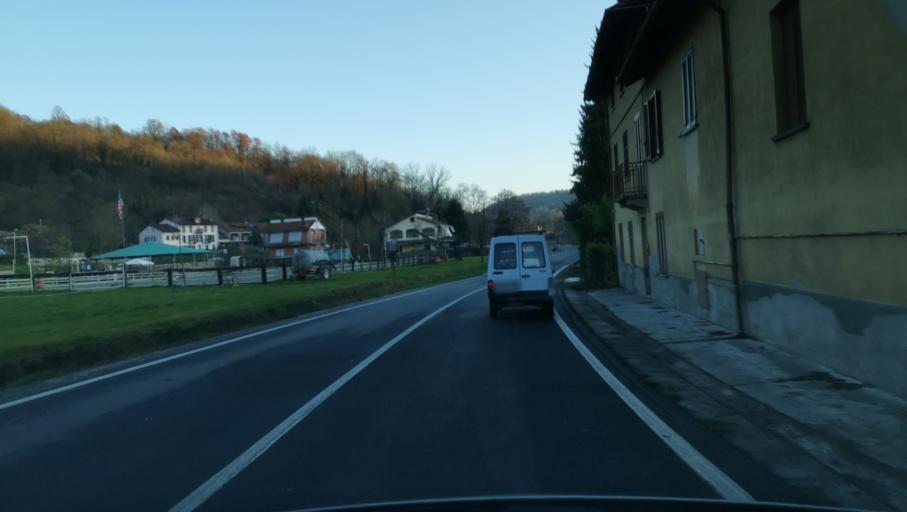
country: IT
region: Piedmont
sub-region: Provincia di Torino
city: San Raffaele Cimena
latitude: 45.1246
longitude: 7.8557
